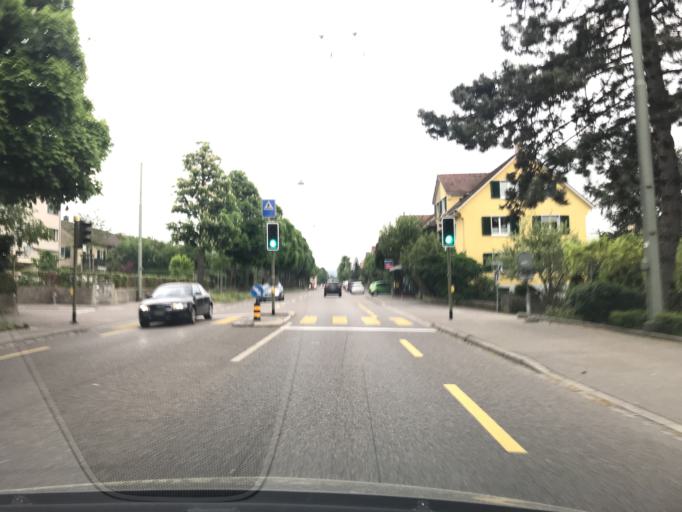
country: CH
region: Zurich
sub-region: Bezirk Winterthur
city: Wuelflingen (Kreis 6) / Lindenplatz
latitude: 47.5099
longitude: 8.7027
